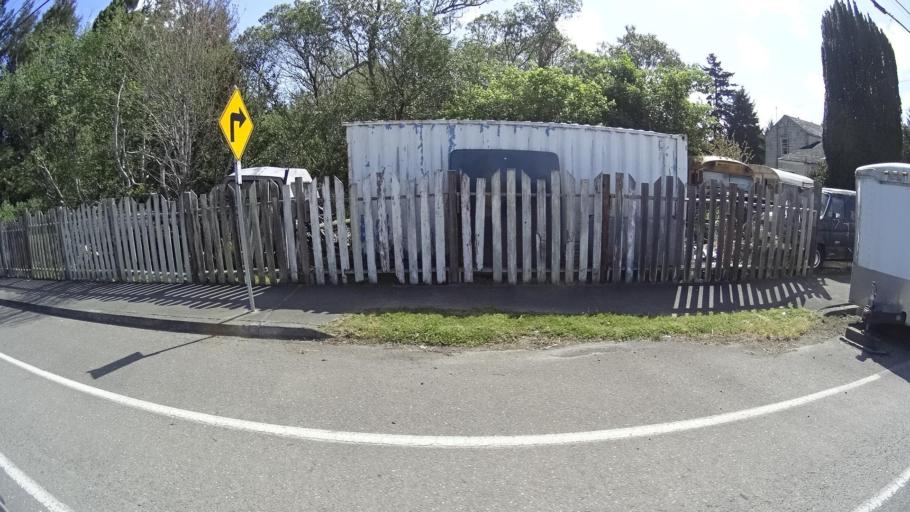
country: US
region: California
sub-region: Humboldt County
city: Cutten
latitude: 40.7633
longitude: -124.1455
